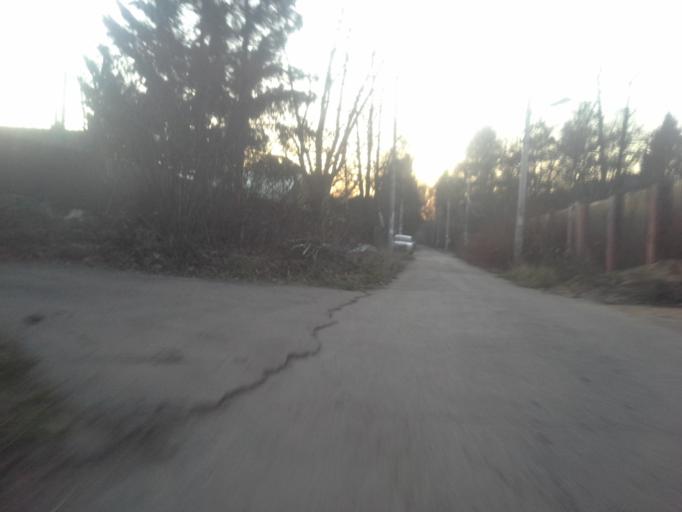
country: RU
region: Moscow
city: Tolstopal'tsevo
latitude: 55.6163
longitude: 37.2205
